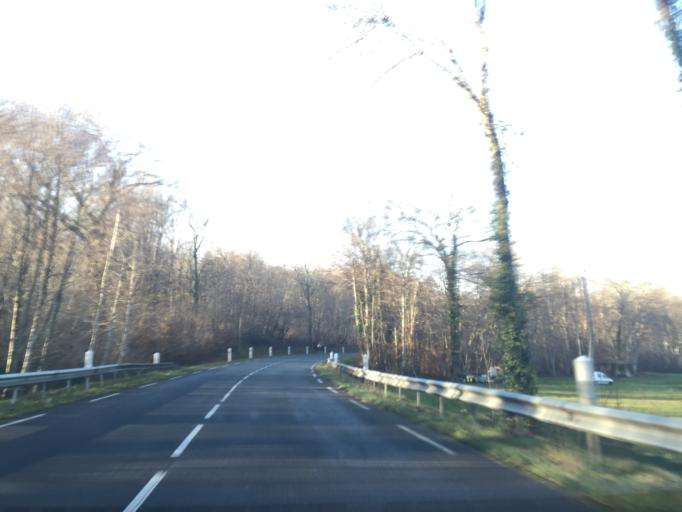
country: FR
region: Aquitaine
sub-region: Departement de la Dordogne
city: Riberac
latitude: 45.1751
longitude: 0.3888
